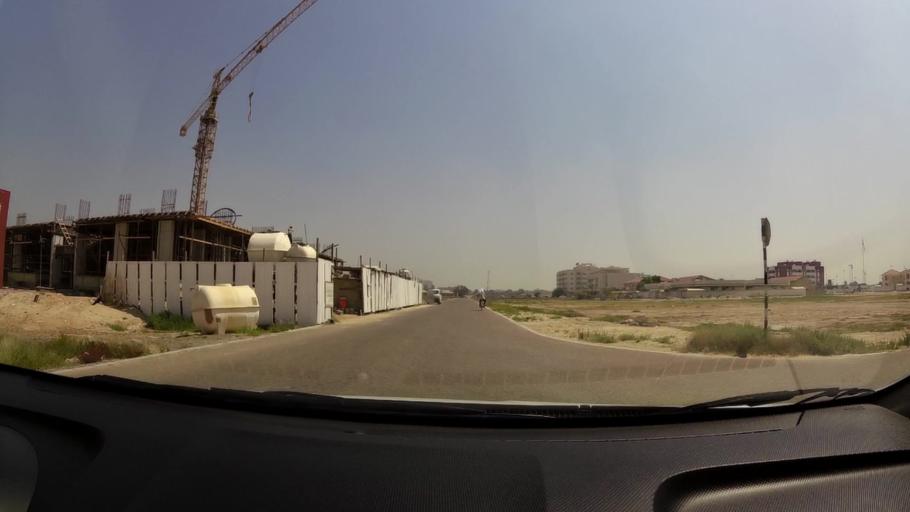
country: AE
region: Umm al Qaywayn
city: Umm al Qaywayn
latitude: 25.5668
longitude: 55.5553
